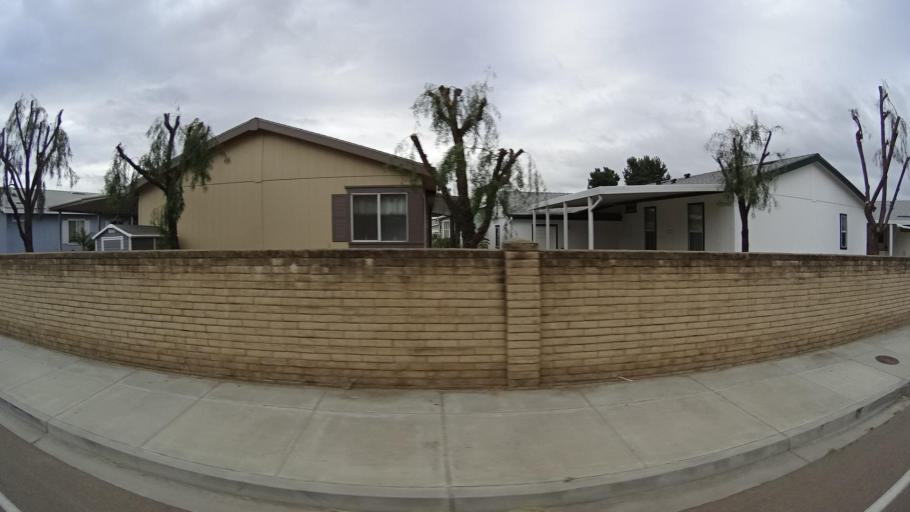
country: US
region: California
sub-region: San Diego County
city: Lakeside
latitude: 32.8644
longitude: -116.9378
